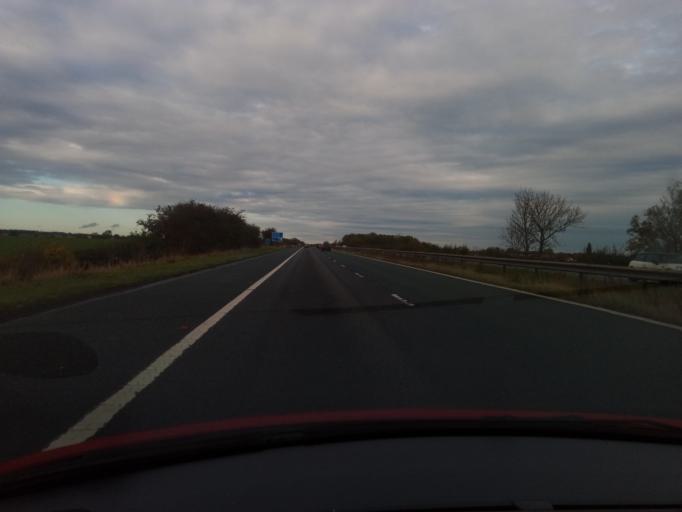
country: GB
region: England
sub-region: Darlington
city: High Coniscliffe
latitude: 54.5384
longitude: -1.6094
